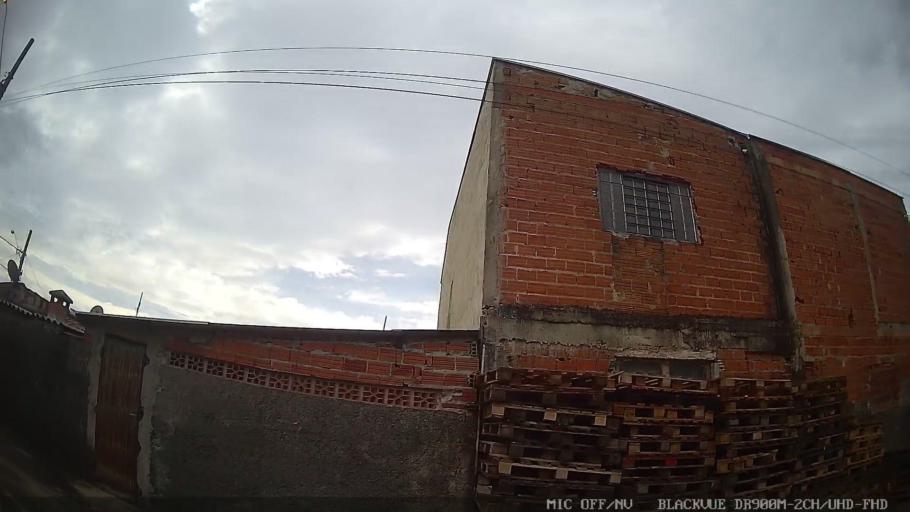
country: BR
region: Sao Paulo
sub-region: Salto
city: Salto
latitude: -23.2225
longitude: -47.2658
